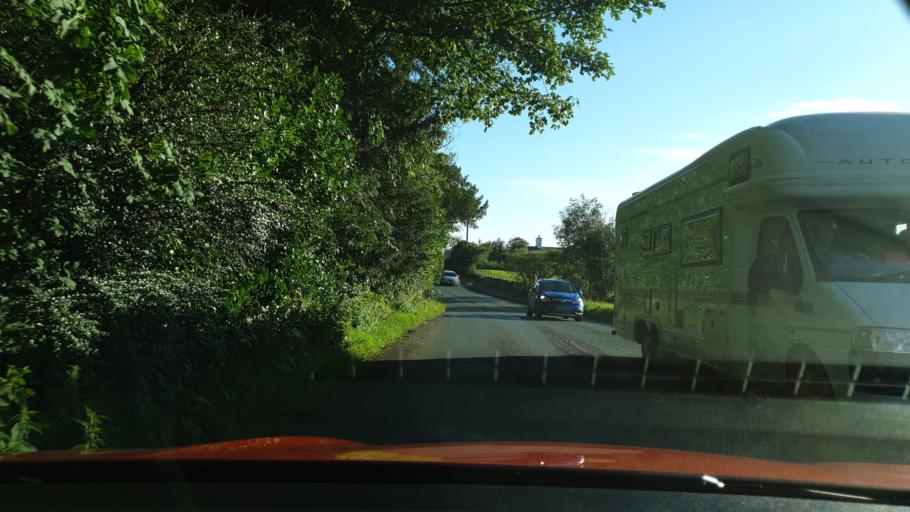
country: GB
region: England
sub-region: Cumbria
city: Windermere
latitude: 54.4015
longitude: -2.9126
